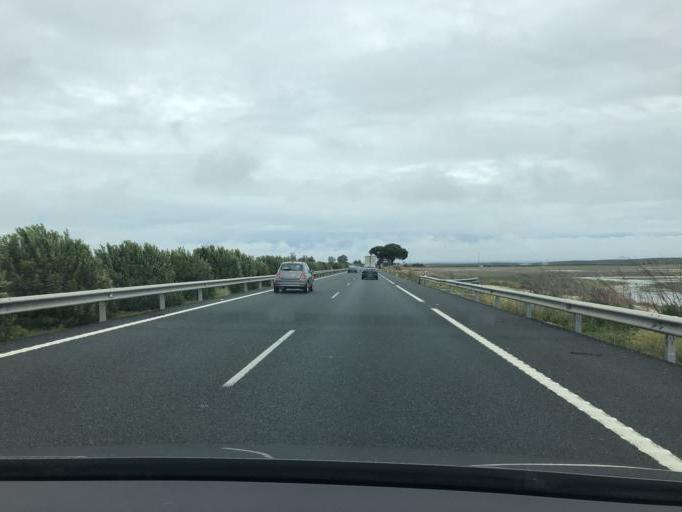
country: ES
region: Andalusia
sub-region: Provincia de Sevilla
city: El Arahal
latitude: 37.2689
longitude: -5.6463
